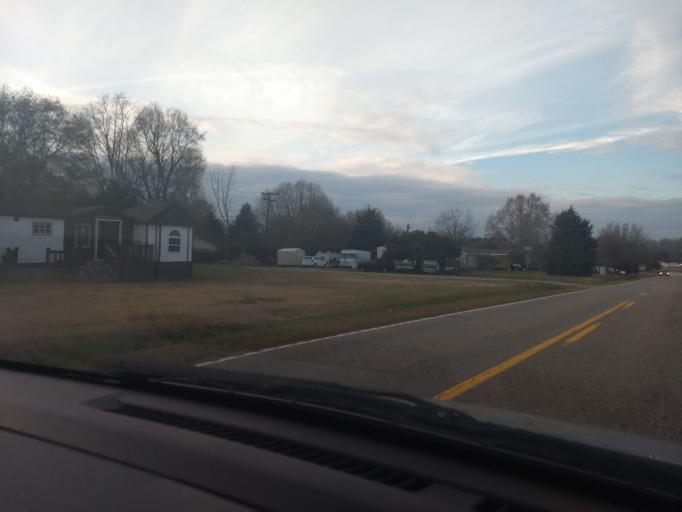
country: US
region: South Carolina
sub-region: Greenville County
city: Greer
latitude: 34.9885
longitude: -82.2019
